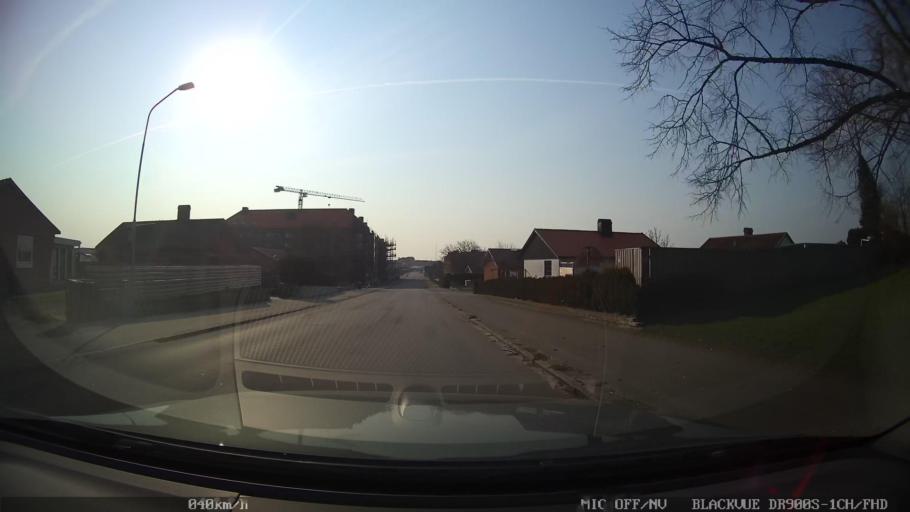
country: SE
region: Skane
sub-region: Ystads Kommun
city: Ystad
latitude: 55.4385
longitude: 13.8299
